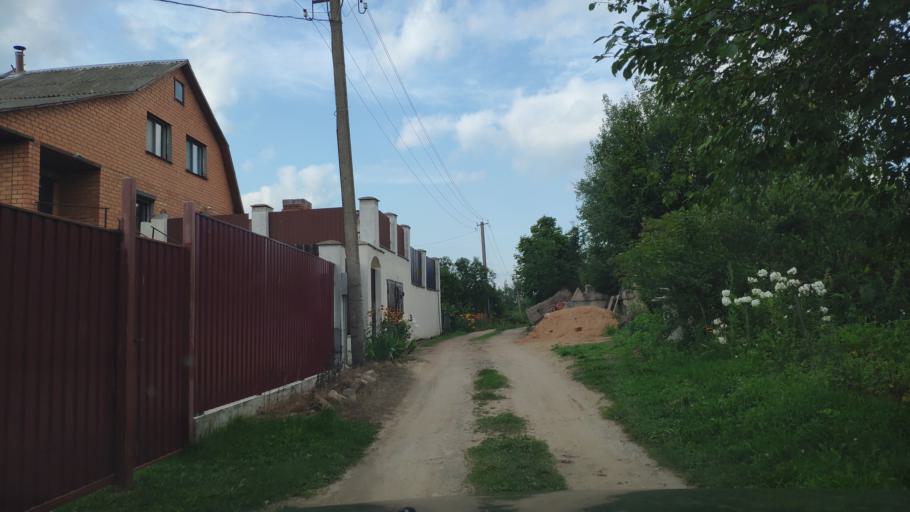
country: BY
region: Minsk
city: Khatsyezhyna
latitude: 53.8577
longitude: 27.2920
